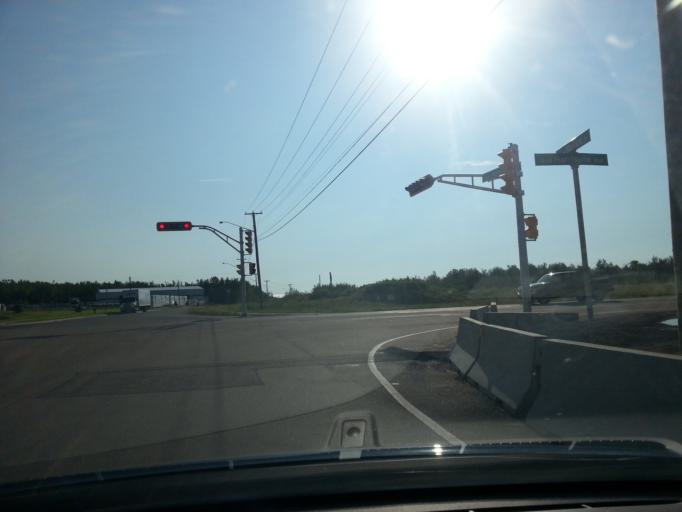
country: CA
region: New Brunswick
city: Dieppe
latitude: 46.1132
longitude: -64.7133
